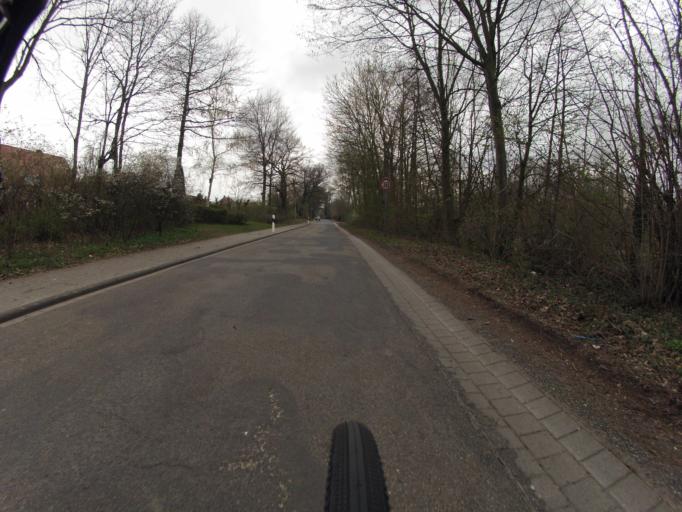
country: DE
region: North Rhine-Westphalia
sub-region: Regierungsbezirk Munster
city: Mettingen
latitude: 52.3246
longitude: 7.7694
